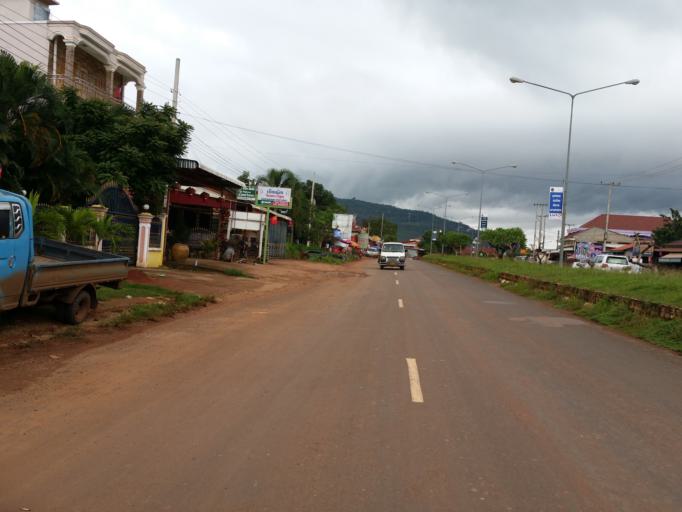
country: LA
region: Champasak
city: Pakxe
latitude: 15.1081
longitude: 105.8392
